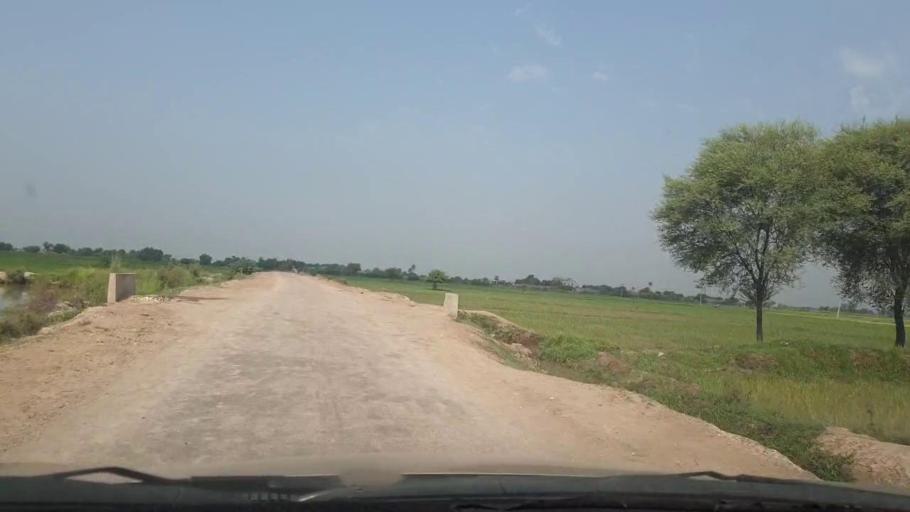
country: PK
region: Sindh
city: Larkana
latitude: 27.6642
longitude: 68.1890
